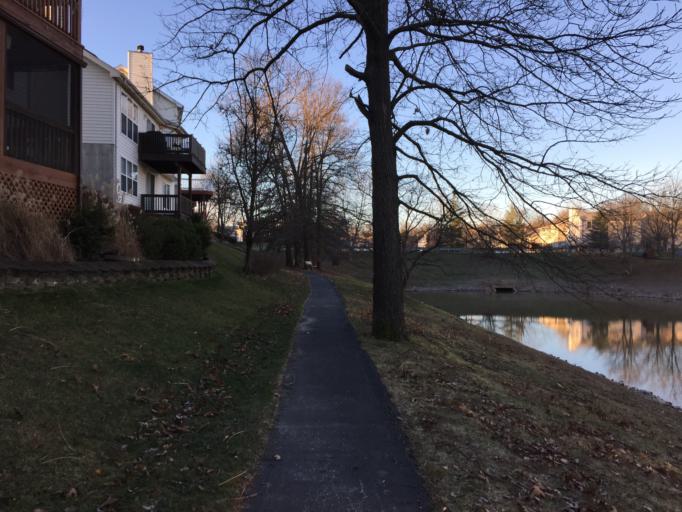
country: US
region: Missouri
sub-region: Saint Louis County
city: Ellisville
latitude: 38.5775
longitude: -90.6127
